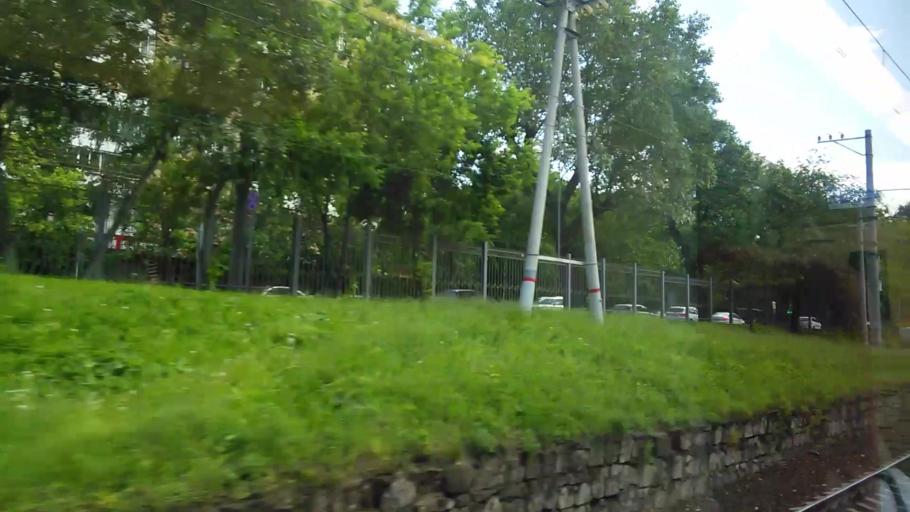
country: RU
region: Moscow
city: Mar'ina Roshcha
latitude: 55.7860
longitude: 37.5872
